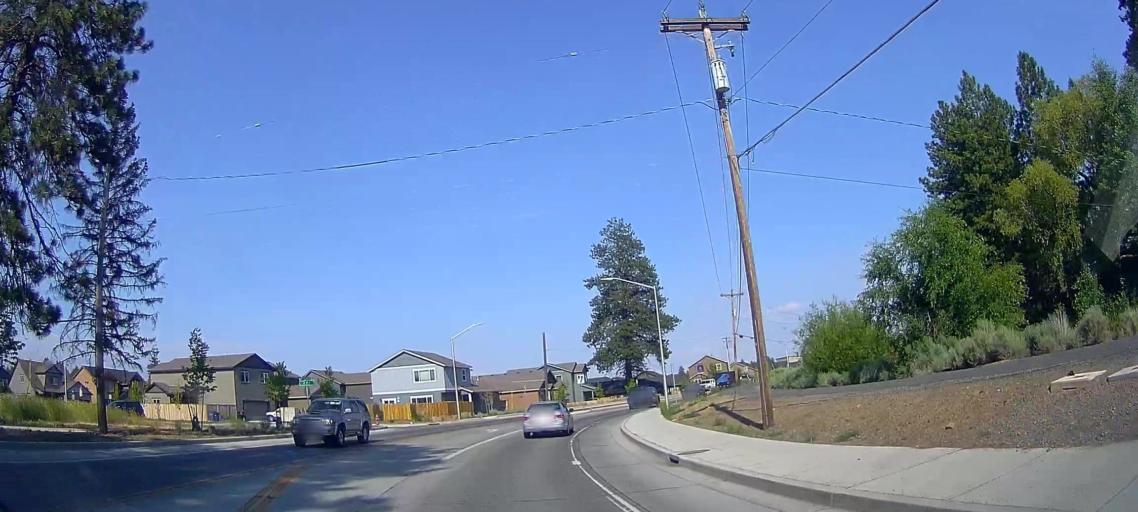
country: US
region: Oregon
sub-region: Deschutes County
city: Bend
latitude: 44.0390
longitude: -121.2990
